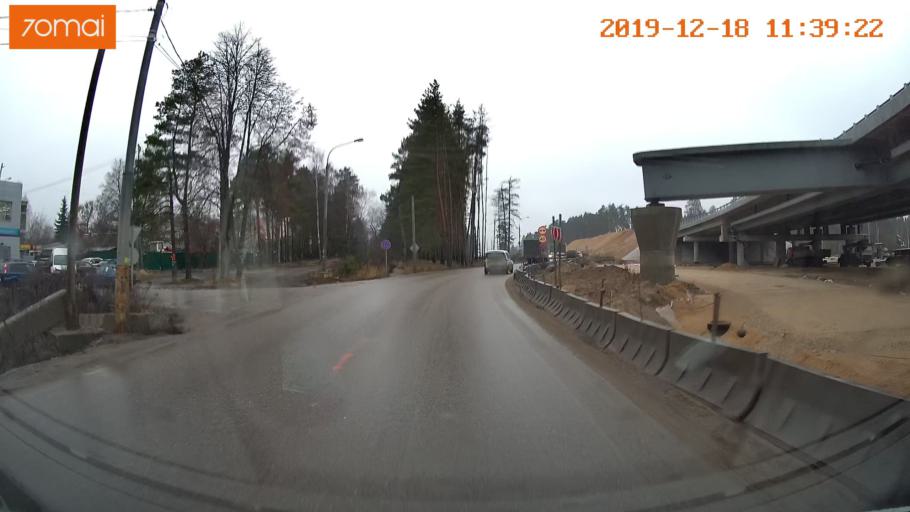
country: RU
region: Moskovskaya
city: Zvenigorod
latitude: 55.7010
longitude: 36.8816
